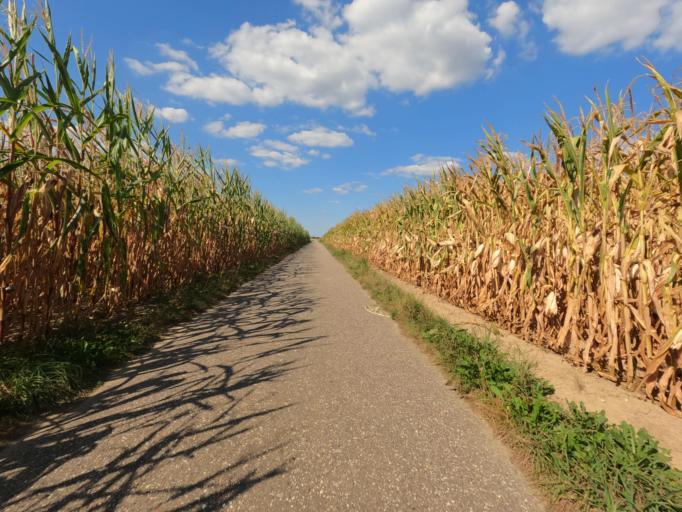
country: DE
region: North Rhine-Westphalia
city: Huckelhoven
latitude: 51.0836
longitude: 6.2388
